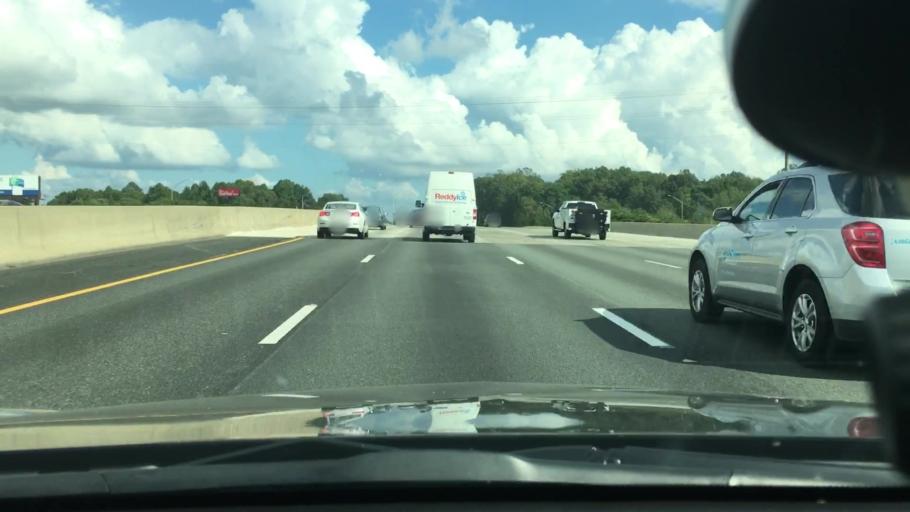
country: US
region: North Carolina
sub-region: Alamance County
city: Graham
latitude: 36.0640
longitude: -79.4316
